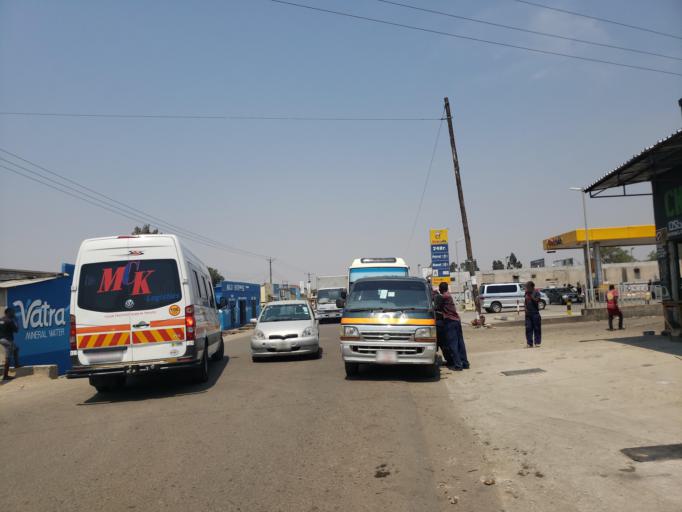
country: ZM
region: Lusaka
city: Lusaka
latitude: -15.4472
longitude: 28.2430
